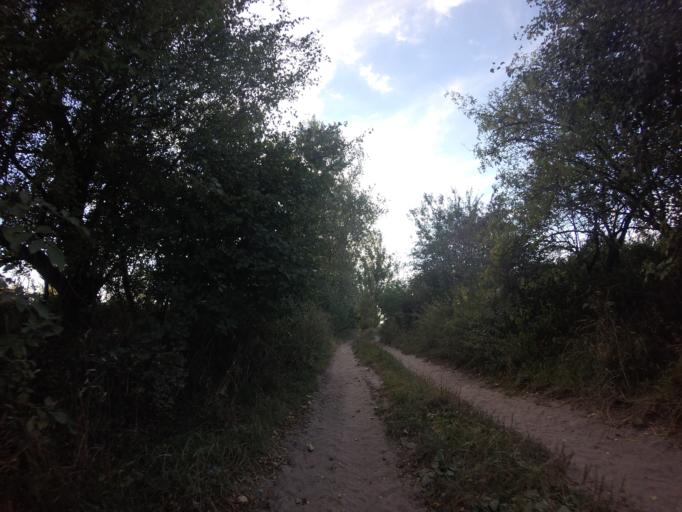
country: PL
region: West Pomeranian Voivodeship
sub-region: Powiat choszczenski
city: Choszczno
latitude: 53.1127
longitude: 15.4383
